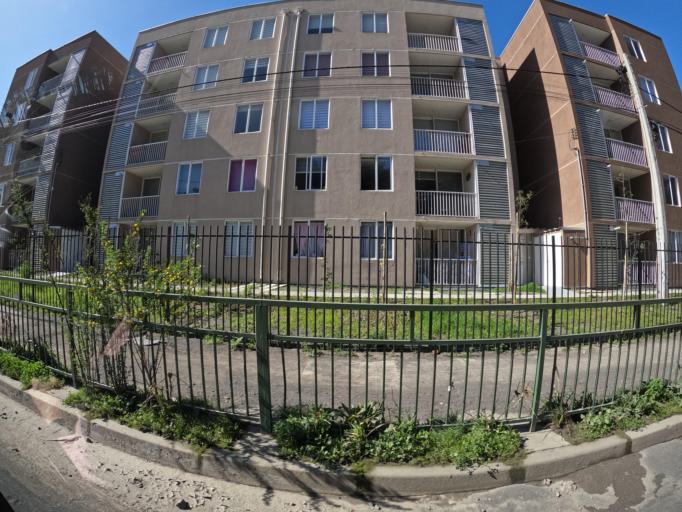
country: CL
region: Biobio
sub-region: Provincia de Concepcion
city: Concepcion
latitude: -36.8824
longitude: -73.1491
